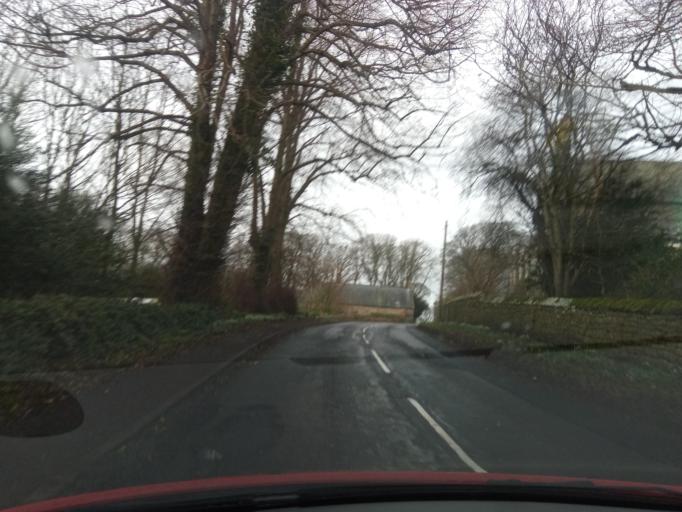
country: GB
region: England
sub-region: Northumberland
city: Rothley
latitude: 55.1643
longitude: -1.9613
